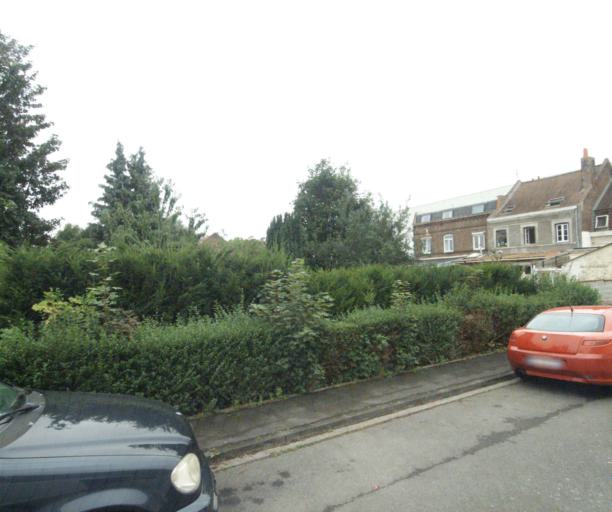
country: FR
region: Nord-Pas-de-Calais
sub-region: Departement du Nord
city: Ronchin
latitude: 50.6055
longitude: 3.0833
